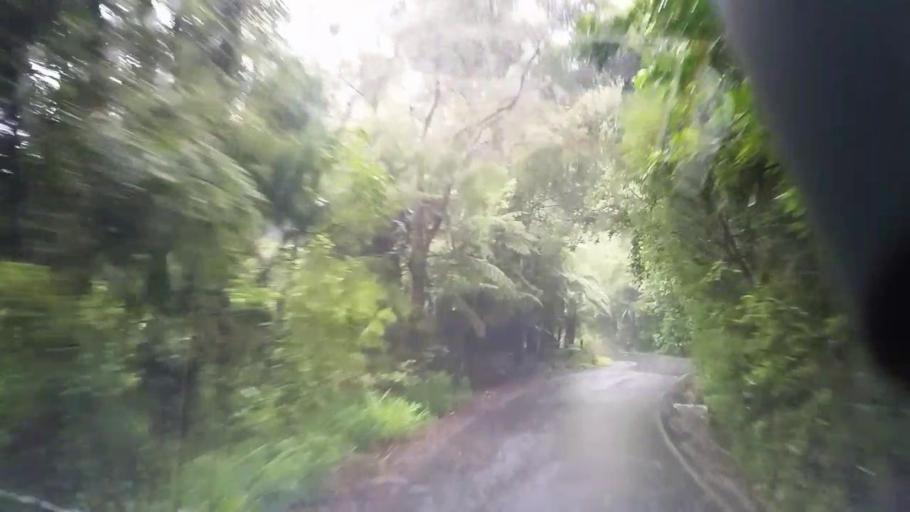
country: NZ
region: Auckland
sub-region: Auckland
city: Waitakere
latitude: -36.9160
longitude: 174.5664
